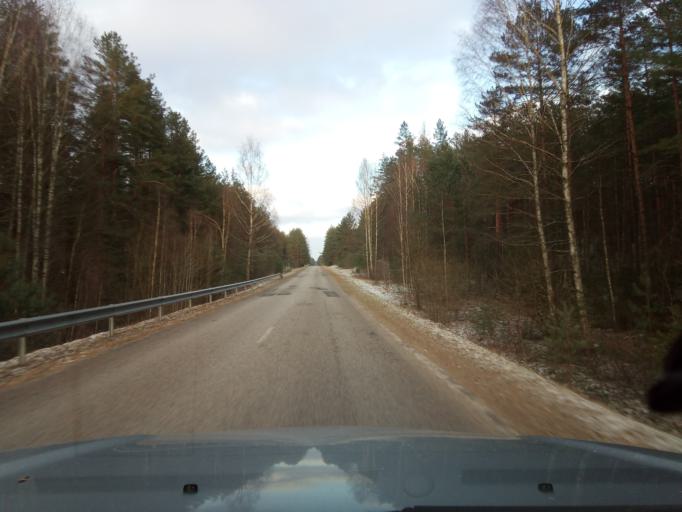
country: LT
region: Alytaus apskritis
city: Varena
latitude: 54.1070
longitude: 24.4357
